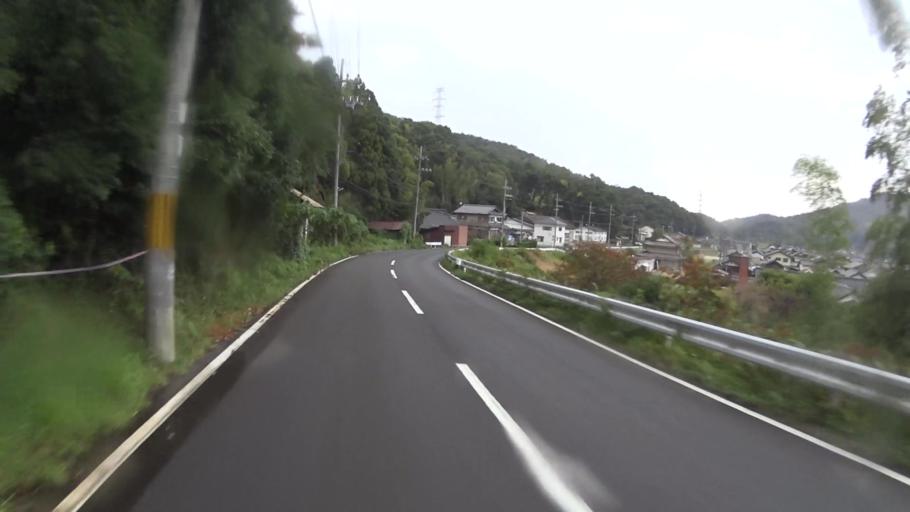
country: JP
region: Kyoto
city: Miyazu
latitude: 35.5606
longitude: 135.2414
